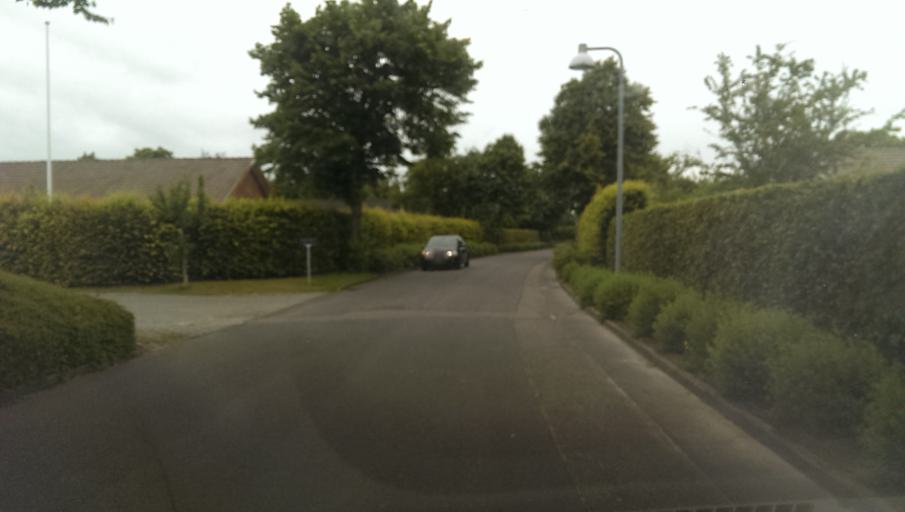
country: DK
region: South Denmark
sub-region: Esbjerg Kommune
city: Bramming
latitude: 55.4796
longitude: 8.6881
